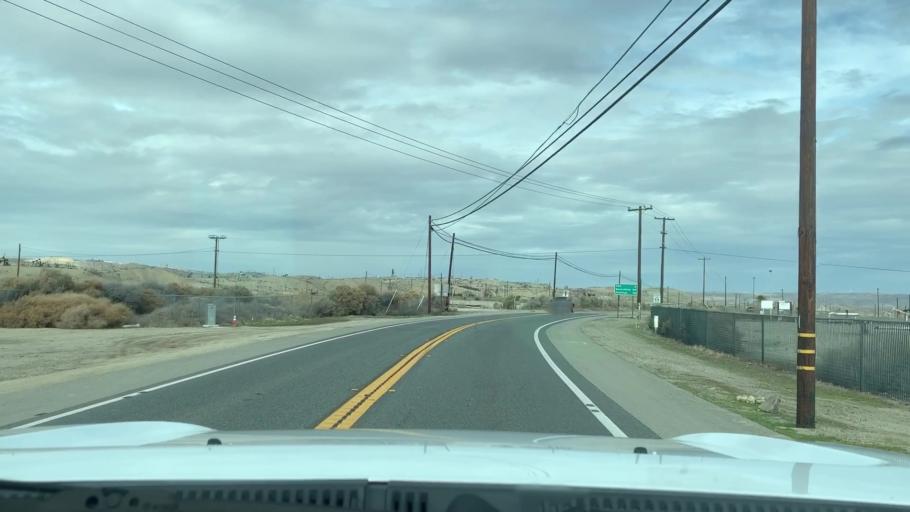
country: US
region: California
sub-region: Kern County
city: Maricopa
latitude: 35.0658
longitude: -119.4018
